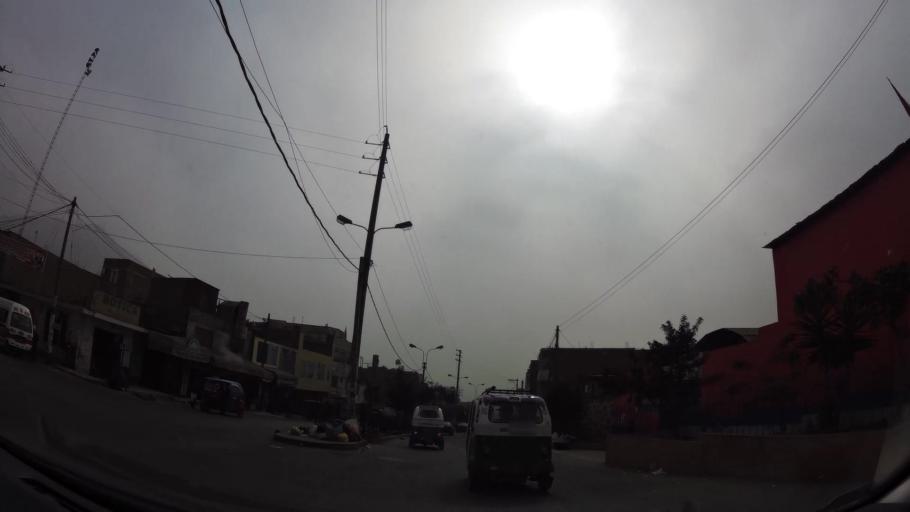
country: PE
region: Lima
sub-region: Lima
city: Chaclacayo
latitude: -12.0159
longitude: -76.8213
